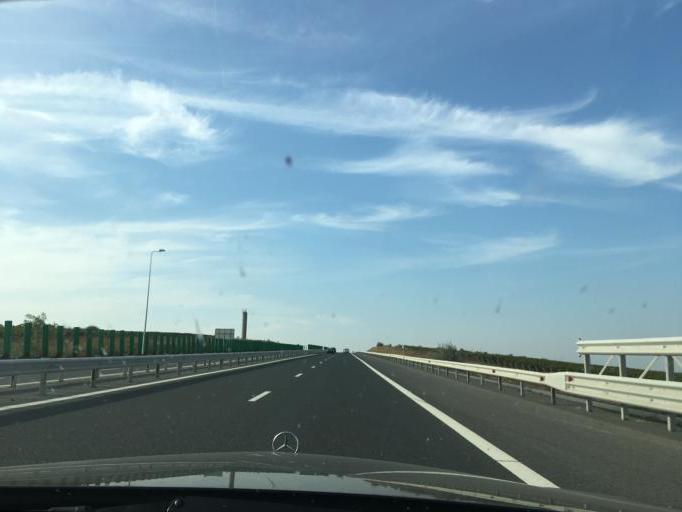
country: RO
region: Constanta
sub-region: Comuna Saligny
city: Saligny
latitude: 44.2865
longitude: 28.0459
